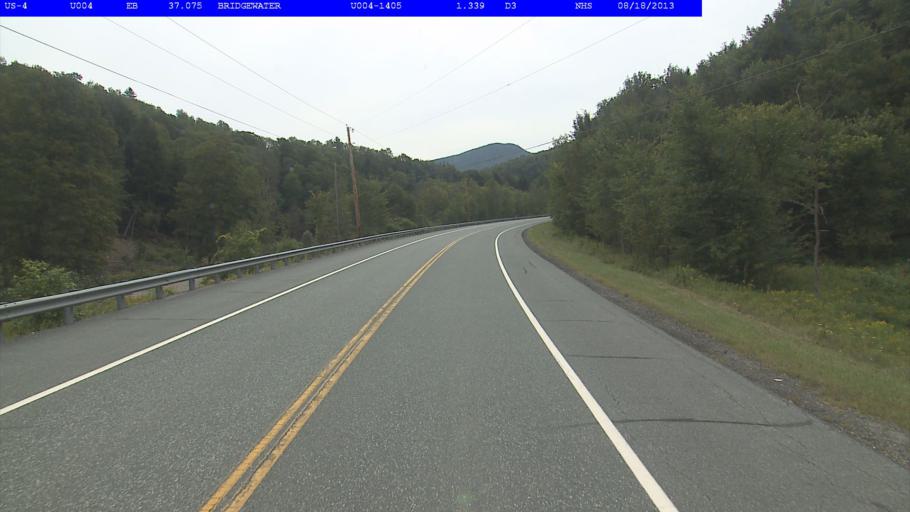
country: US
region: Vermont
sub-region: Windsor County
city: Woodstock
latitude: 43.6020
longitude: -72.7254
